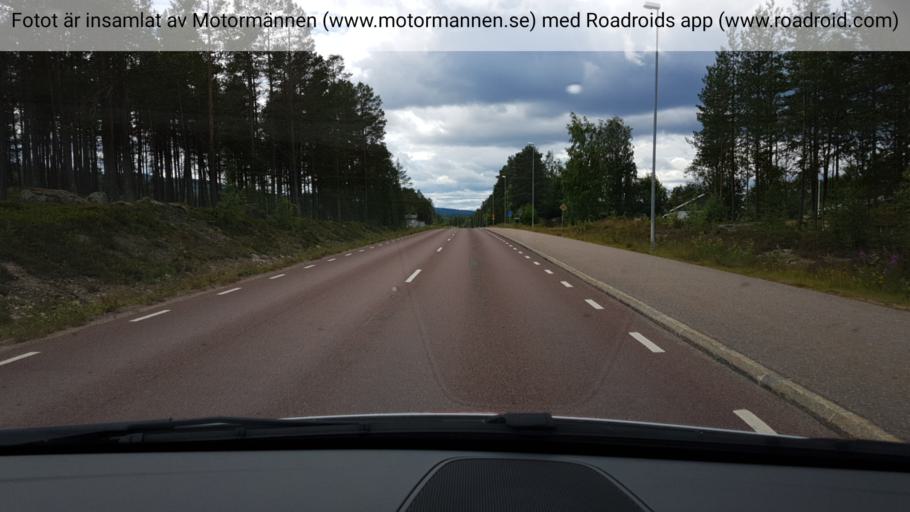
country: SE
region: Jaemtland
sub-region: Harjedalens Kommun
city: Sveg
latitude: 62.0226
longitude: 14.3707
